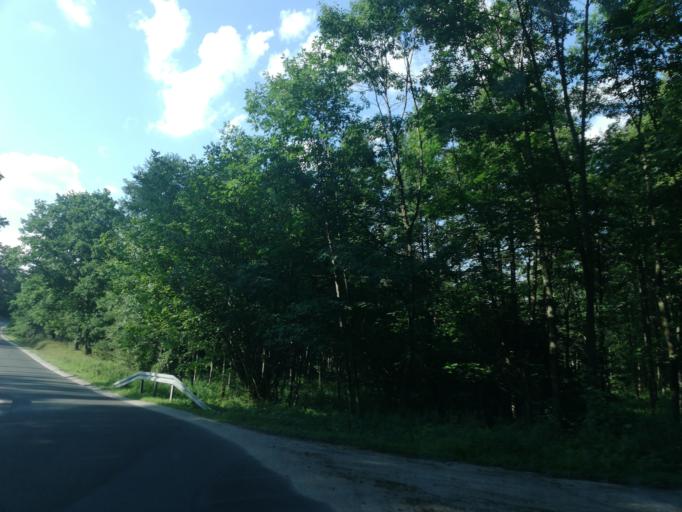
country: PL
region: Kujawsko-Pomorskie
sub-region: Powiat golubsko-dobrzynski
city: Ciechocin
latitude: 53.0876
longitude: 18.9439
